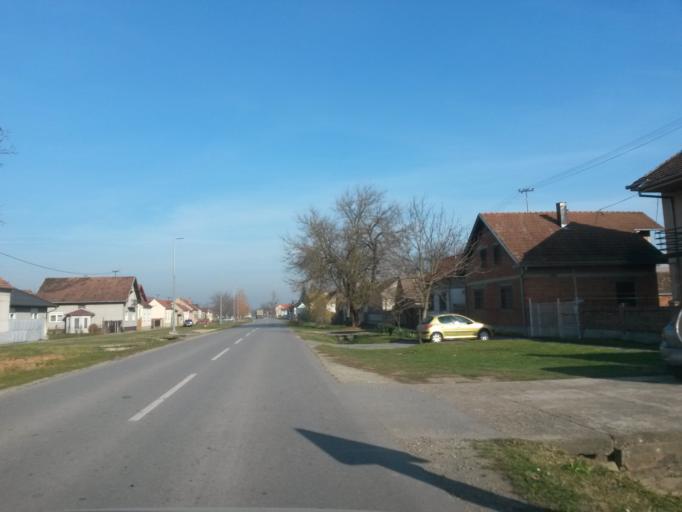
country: HR
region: Vukovarsko-Srijemska
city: Privlaka
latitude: 45.2002
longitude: 18.8449
